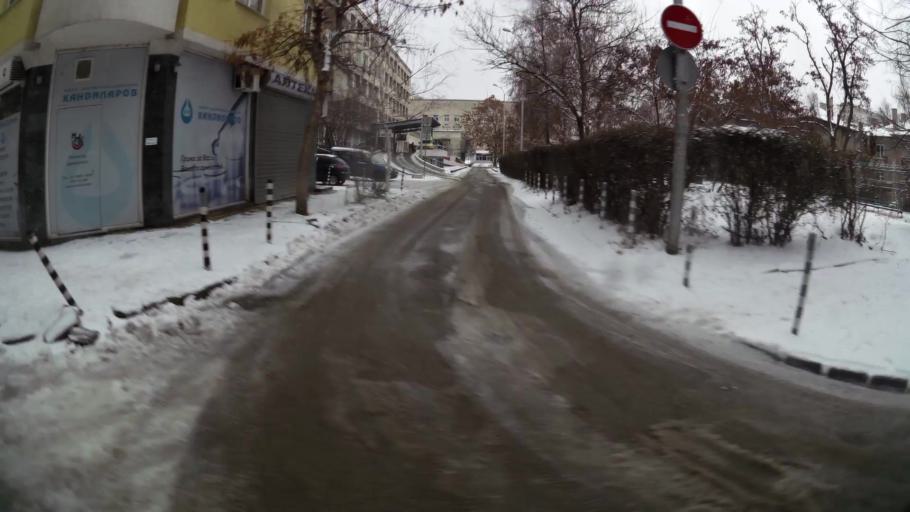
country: BG
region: Sofia-Capital
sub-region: Stolichna Obshtina
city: Sofia
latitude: 42.7005
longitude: 23.3374
